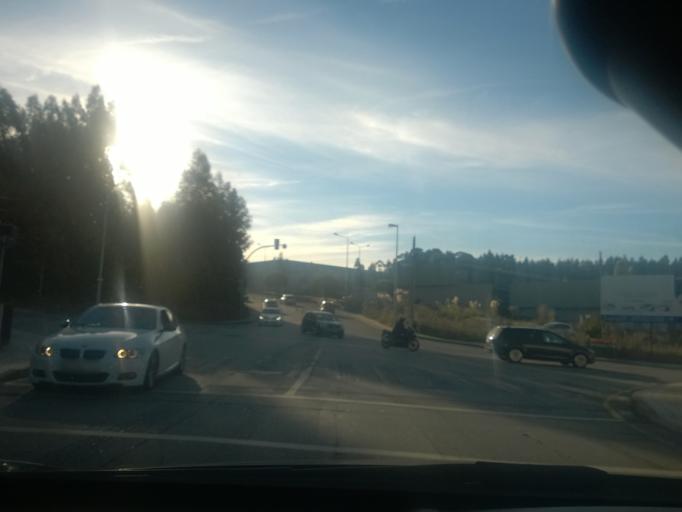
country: PT
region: Porto
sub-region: Maia
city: Anta
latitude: 41.2677
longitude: -8.6186
